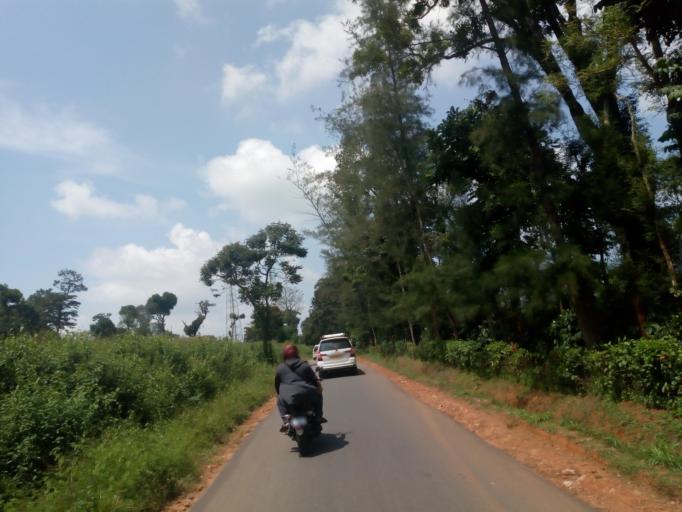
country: IN
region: Karnataka
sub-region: Kodagu
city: Ponnampet
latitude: 12.0318
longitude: 75.9550
